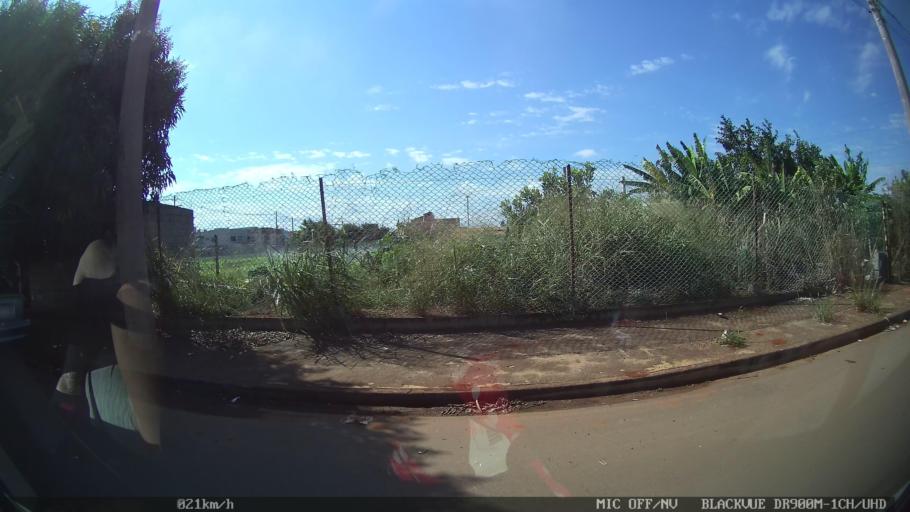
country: BR
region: Sao Paulo
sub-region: Americana
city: Americana
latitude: -22.7209
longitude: -47.3187
